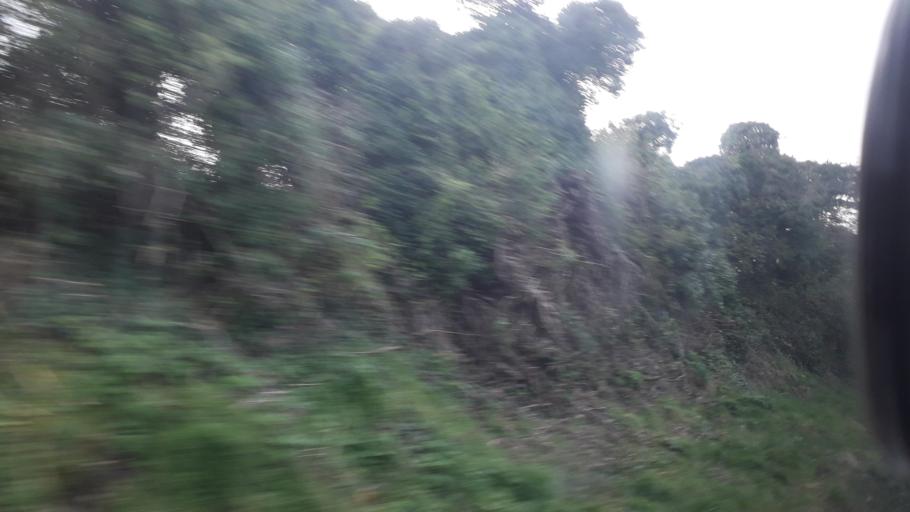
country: IE
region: Leinster
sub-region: An Mhi
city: Enfield
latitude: 53.4159
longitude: -6.8805
